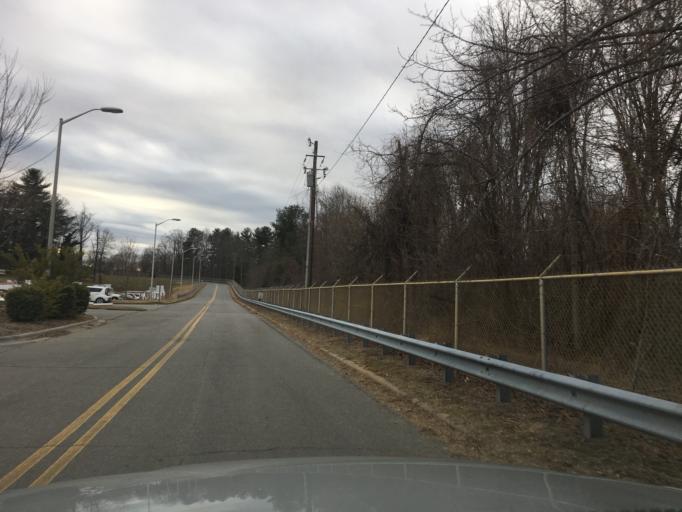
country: US
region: North Carolina
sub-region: Buncombe County
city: Woodfin
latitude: 35.6078
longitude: -82.5835
